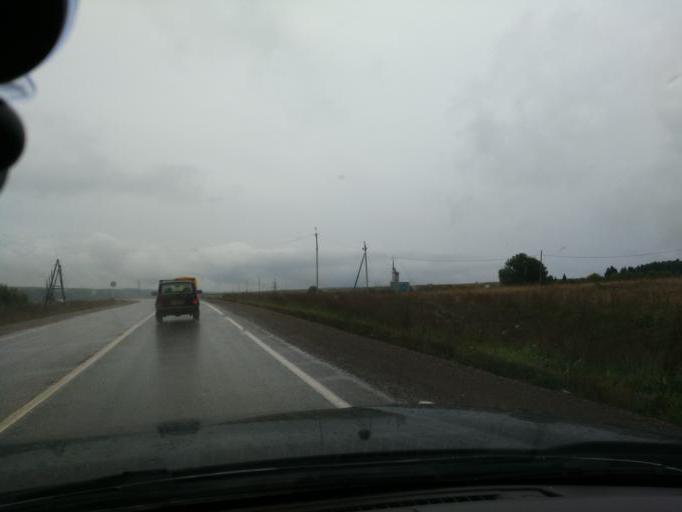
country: RU
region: Perm
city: Yugo-Kamskiy
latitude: 57.6982
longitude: 55.6196
